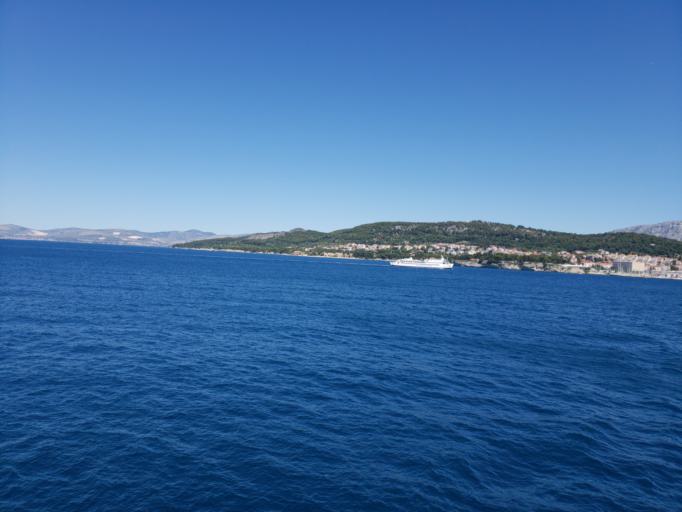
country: HR
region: Splitsko-Dalmatinska
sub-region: Grad Split
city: Split
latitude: 43.4917
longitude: 16.4331
